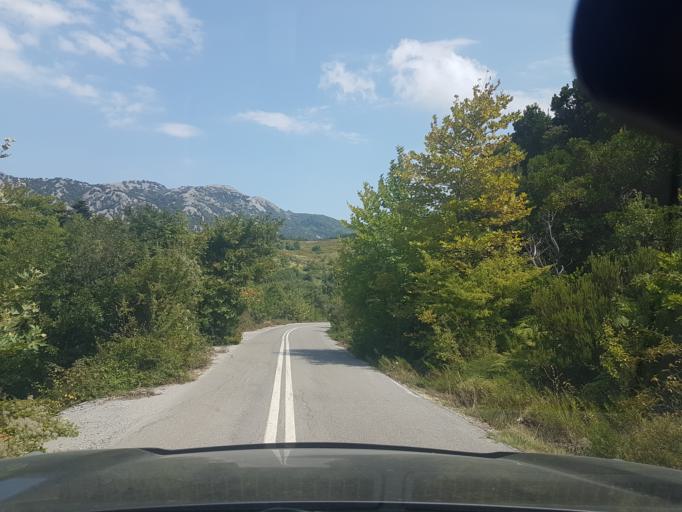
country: GR
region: Central Greece
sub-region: Nomos Evvoias
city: Kymi
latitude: 38.6496
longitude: 24.0322
